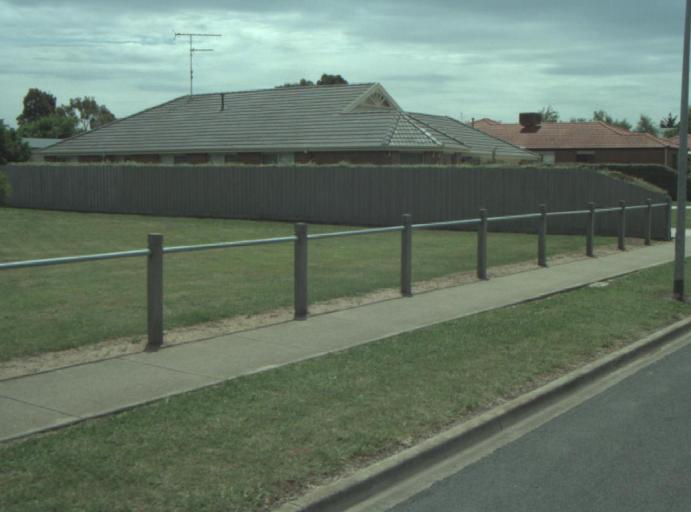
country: AU
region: Victoria
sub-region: Greater Geelong
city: Leopold
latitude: -38.1826
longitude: 144.4752
